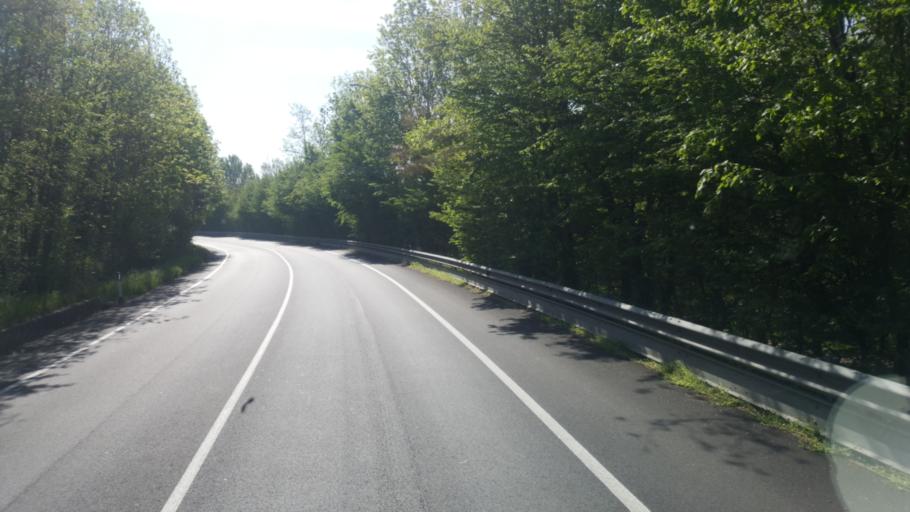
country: IT
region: Lombardy
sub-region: Provincia di Varese
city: Bodio
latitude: 45.8120
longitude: 8.7644
